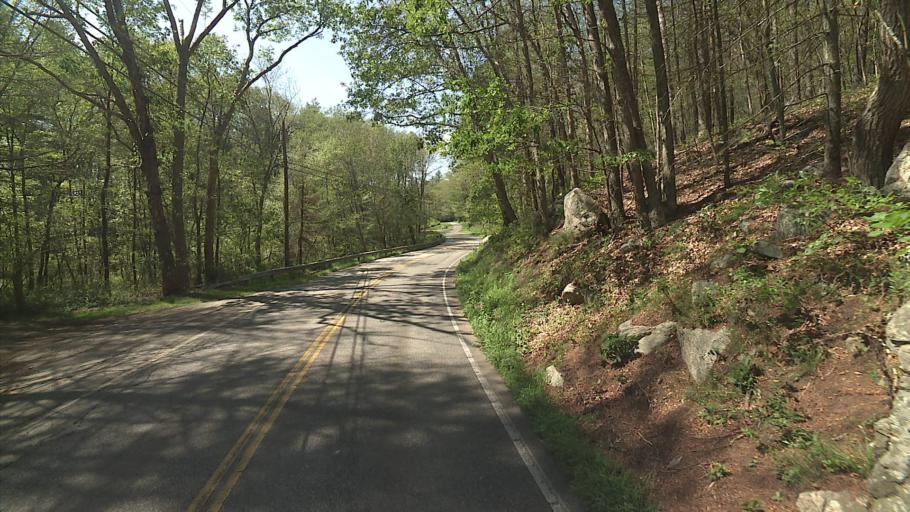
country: US
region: Connecticut
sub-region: Tolland County
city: Mansfield City
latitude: 41.8100
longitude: -72.1692
